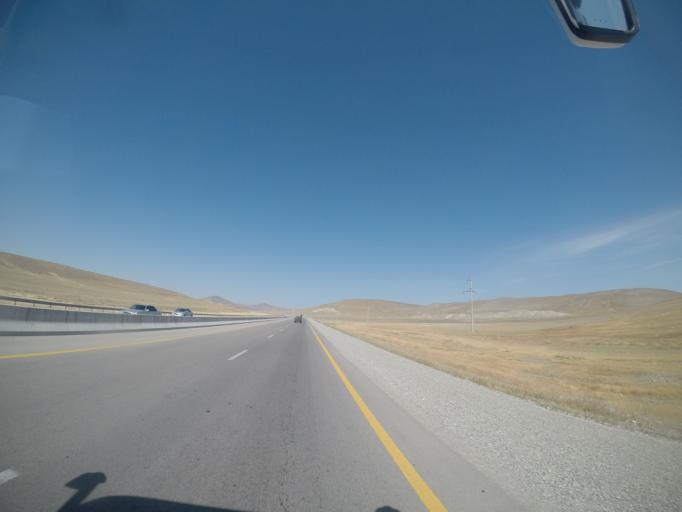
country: AZ
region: Sumqayit
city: Haci Zeynalabdin
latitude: 40.4944
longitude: 49.3628
